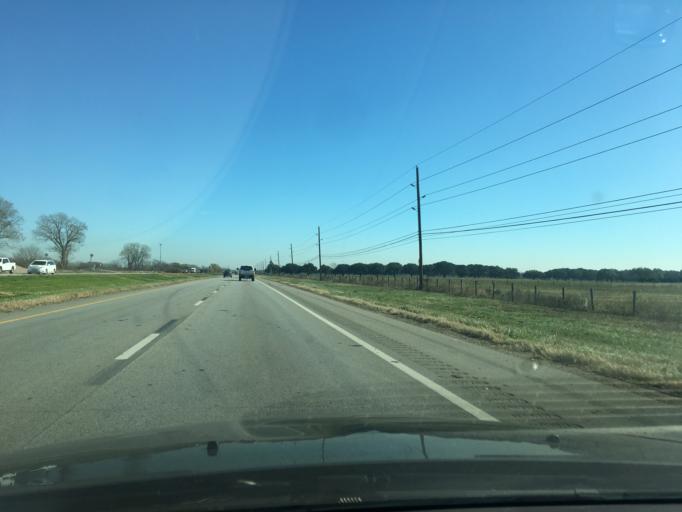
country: US
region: Texas
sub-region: Fort Bend County
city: Pecan Grove
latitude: 29.5972
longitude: -95.7270
